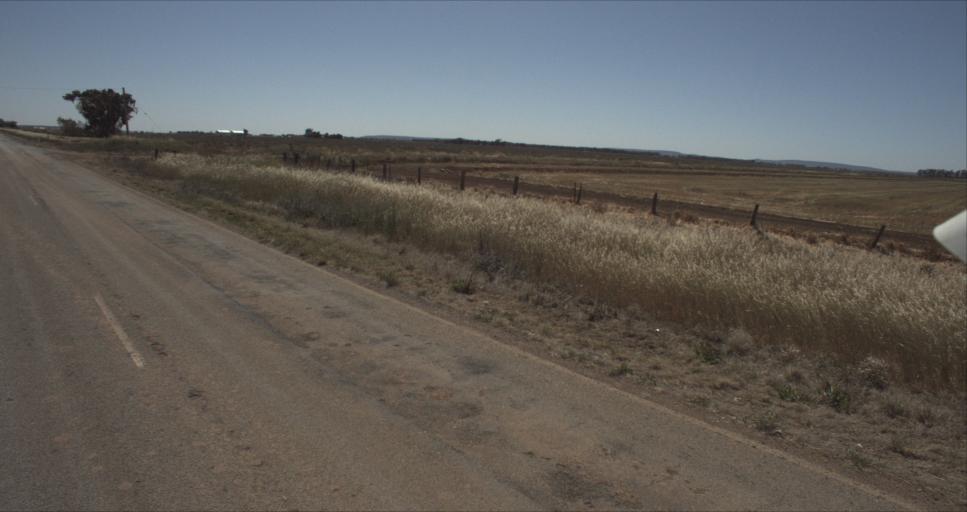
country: AU
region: New South Wales
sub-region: Leeton
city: Leeton
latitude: -34.5147
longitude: 146.2844
